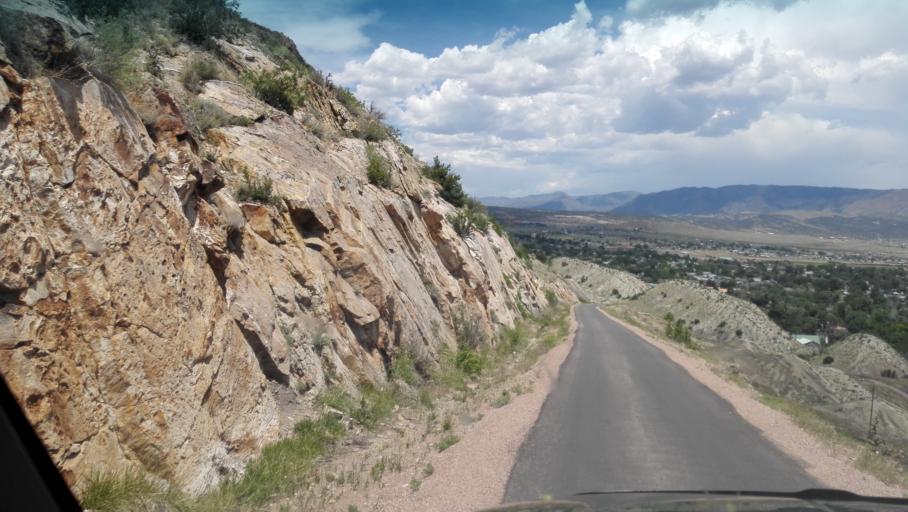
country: US
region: Colorado
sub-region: Fremont County
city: Canon City
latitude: 38.4469
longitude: -105.2487
